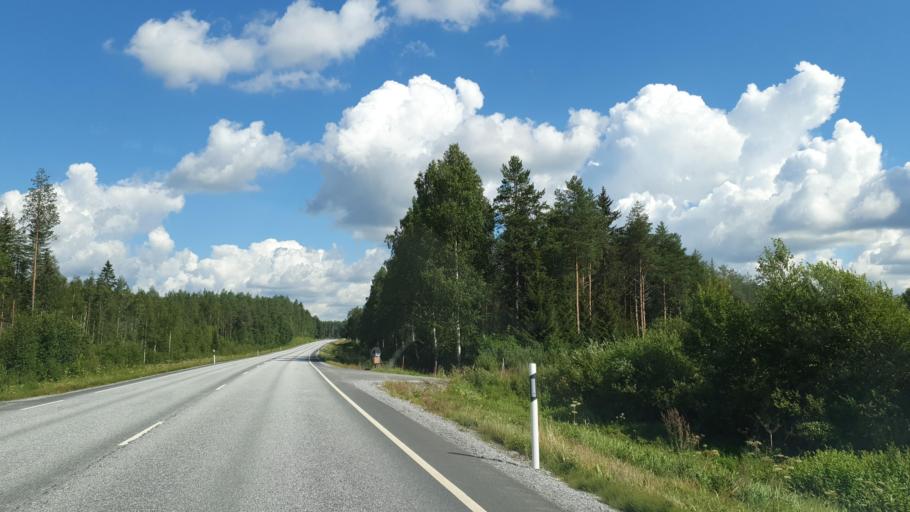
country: FI
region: Northern Savo
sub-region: Ylae-Savo
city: Sonkajaervi
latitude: 63.8378
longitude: 27.4254
